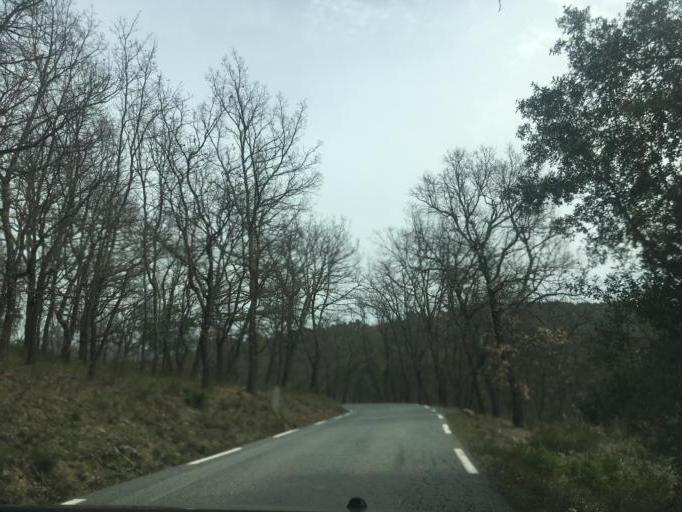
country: FR
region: Provence-Alpes-Cote d'Azur
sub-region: Departement du Var
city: Saint-Paul-en-Foret
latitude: 43.5819
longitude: 6.7272
